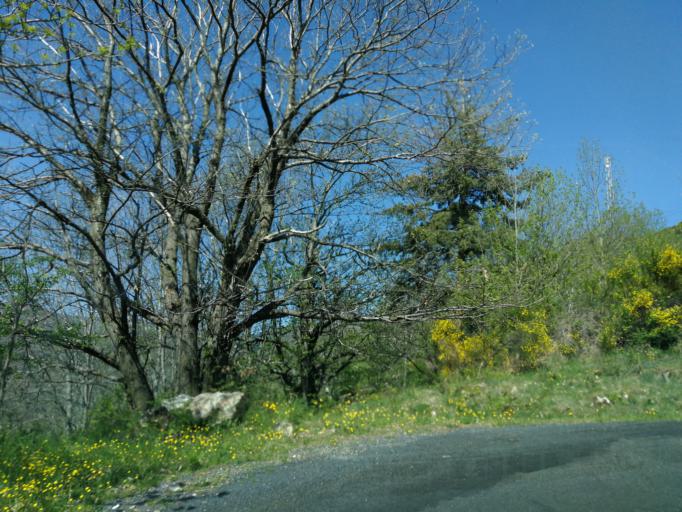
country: FR
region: Rhone-Alpes
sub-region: Departement de l'Ardeche
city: Le Cheylard
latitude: 44.9170
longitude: 4.4262
